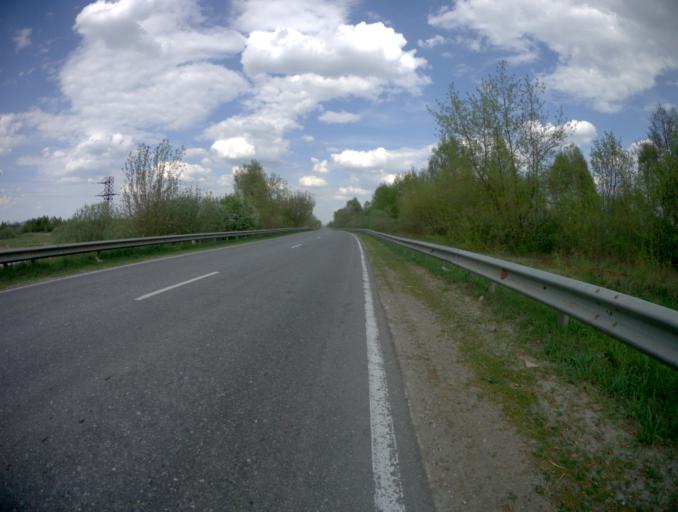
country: RU
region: Vladimir
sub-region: Kovrovskiy Rayon
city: Kovrov
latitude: 56.4359
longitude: 41.2592
